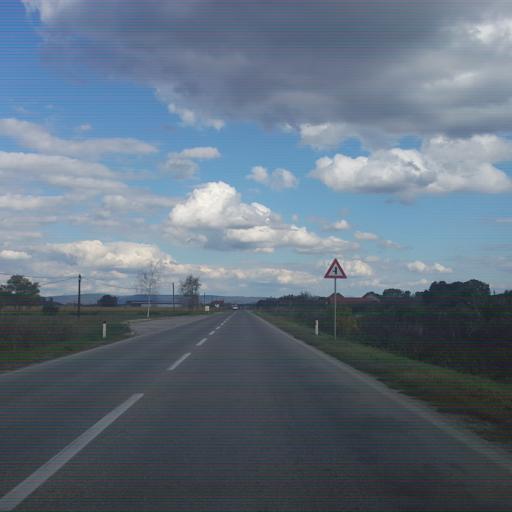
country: RS
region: Central Serbia
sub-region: Rasinski Okrug
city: Krusevac
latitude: 43.5808
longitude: 21.2021
